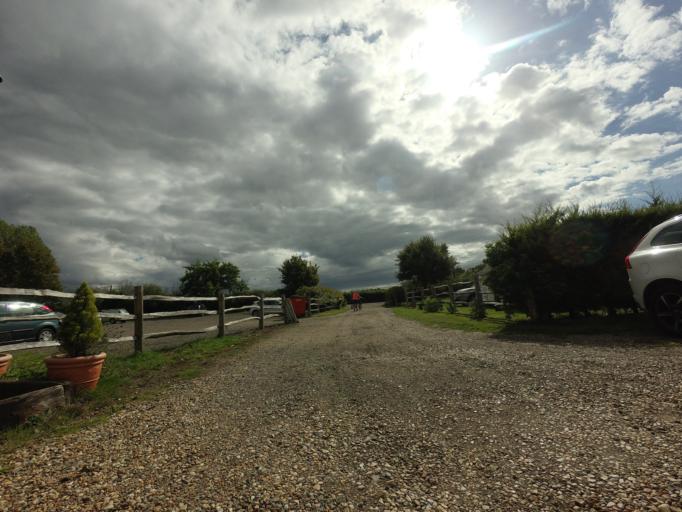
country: GB
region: England
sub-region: Kent
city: Marden
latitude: 51.1610
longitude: 0.4386
